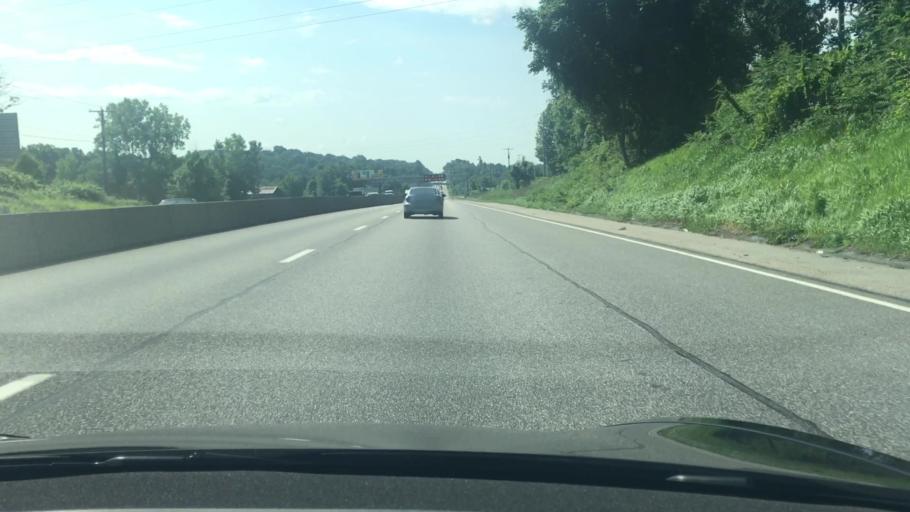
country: US
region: Pennsylvania
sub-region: York County
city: Valley Green
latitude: 40.1274
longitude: -76.7926
